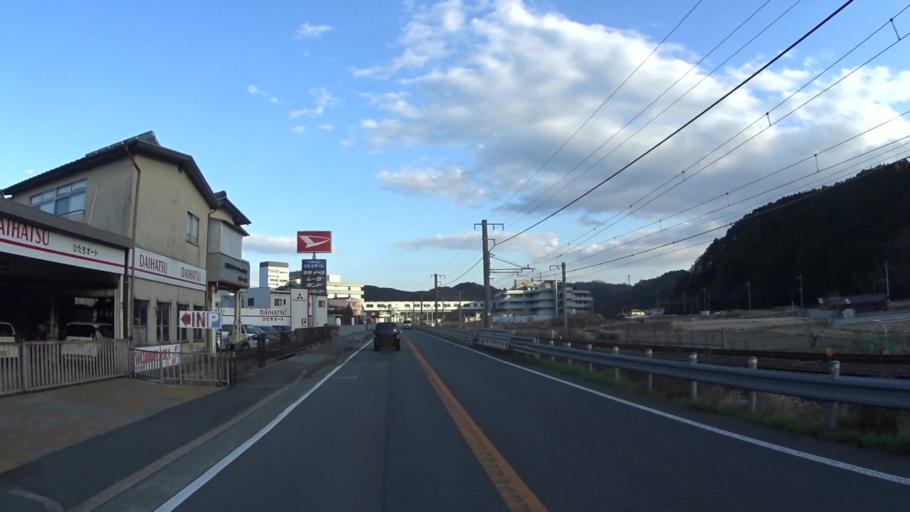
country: JP
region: Kyoto
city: Kameoka
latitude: 35.0657
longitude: 135.5397
